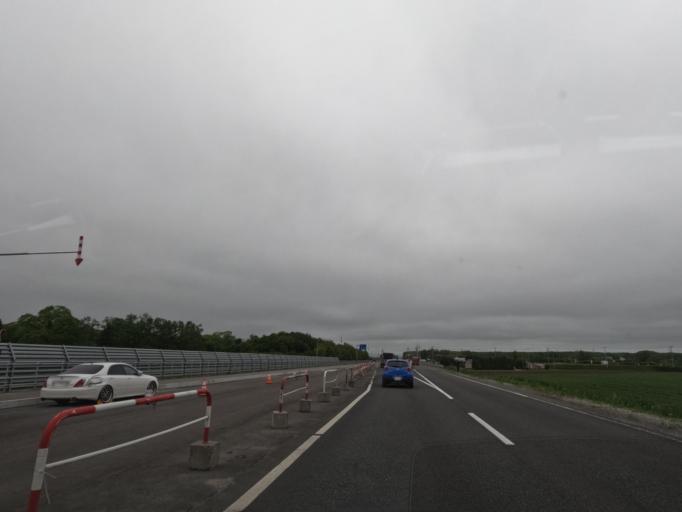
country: JP
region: Hokkaido
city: Ebetsu
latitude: 43.1424
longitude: 141.5165
